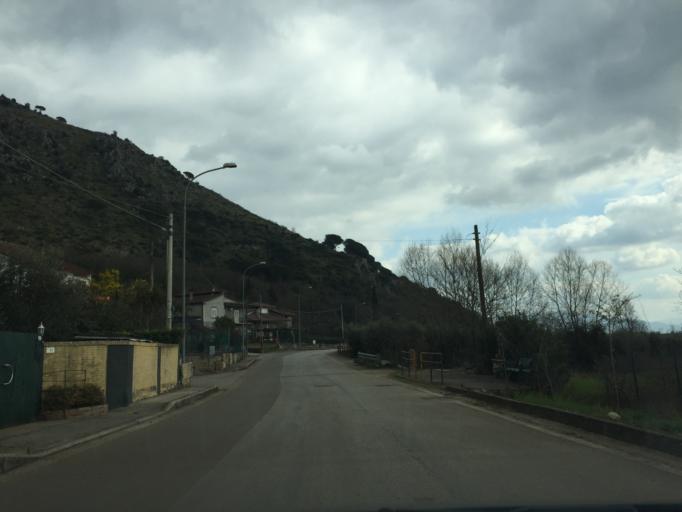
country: IT
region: Latium
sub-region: Provincia di Frosinone
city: Villa Santa Lucia
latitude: 41.4935
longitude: 13.7796
